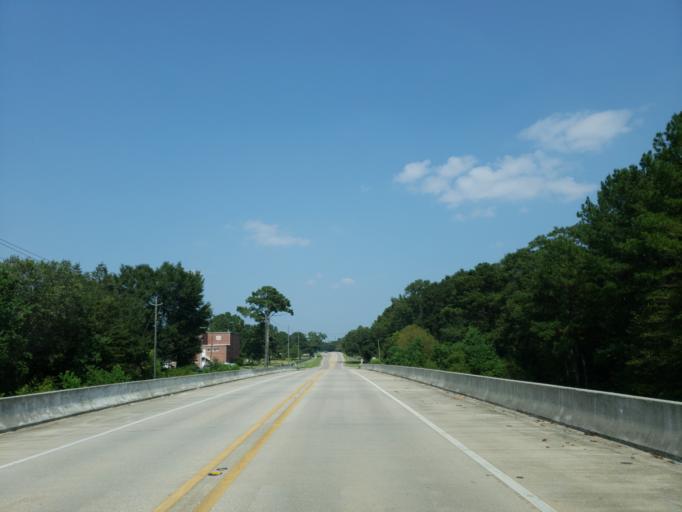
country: US
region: Mississippi
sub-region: Jones County
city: Ellisville
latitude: 31.5842
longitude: -89.2203
